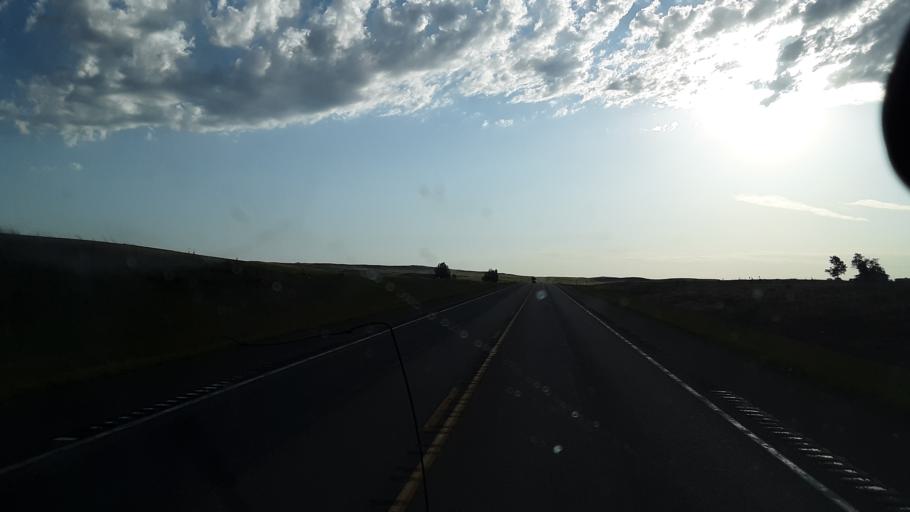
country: US
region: Montana
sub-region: Rosebud County
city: Lame Deer
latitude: 45.5288
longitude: -106.9838
